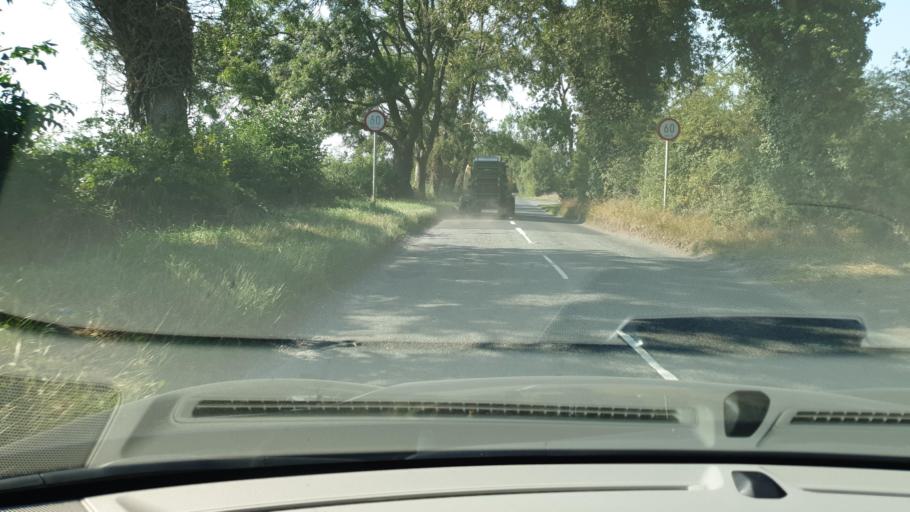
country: IE
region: Leinster
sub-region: An Mhi
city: Athboy
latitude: 53.6168
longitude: -6.9061
